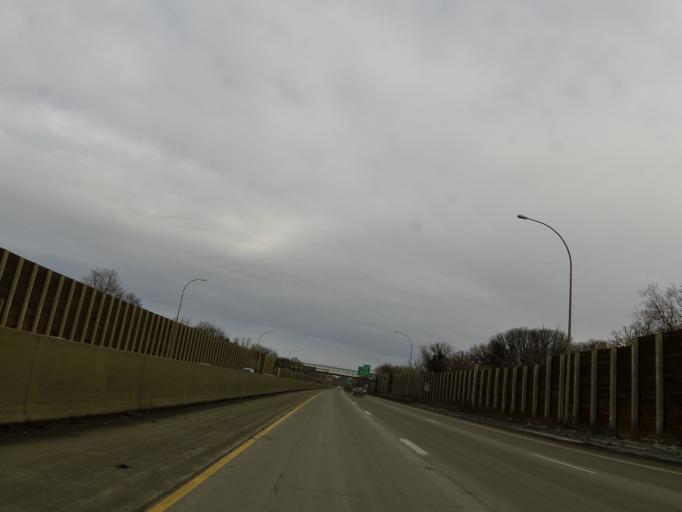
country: US
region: Minnesota
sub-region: Hennepin County
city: Richfield
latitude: 44.8691
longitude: -93.2990
